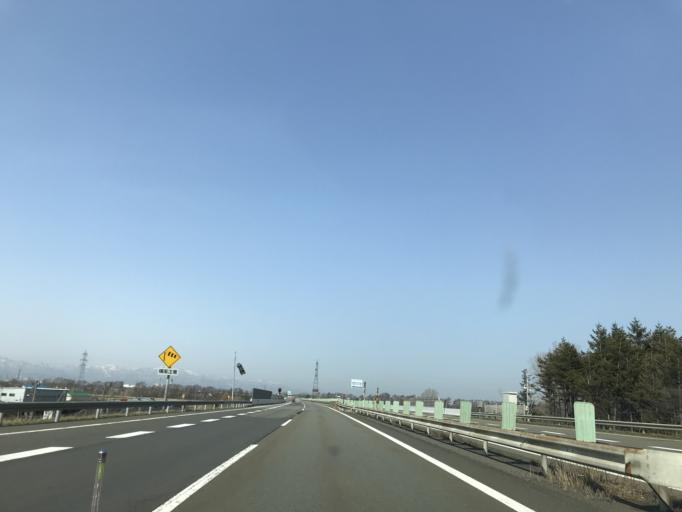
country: JP
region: Hokkaido
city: Ebetsu
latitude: 43.0942
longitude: 141.4930
